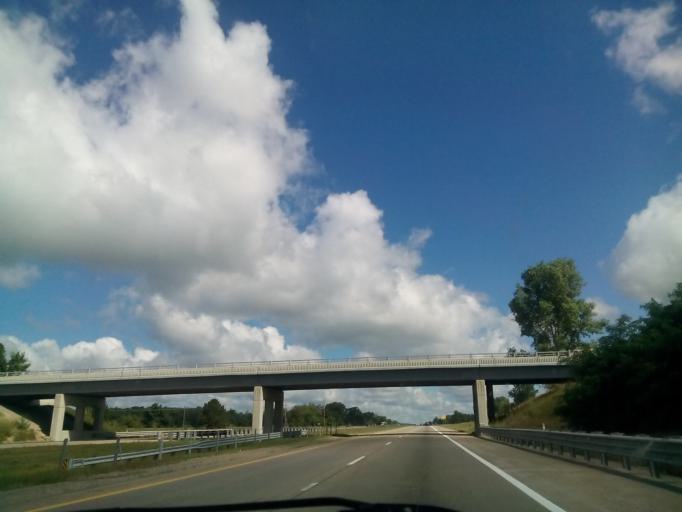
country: US
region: Michigan
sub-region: Genesee County
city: Fenton
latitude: 42.6762
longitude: -83.7596
